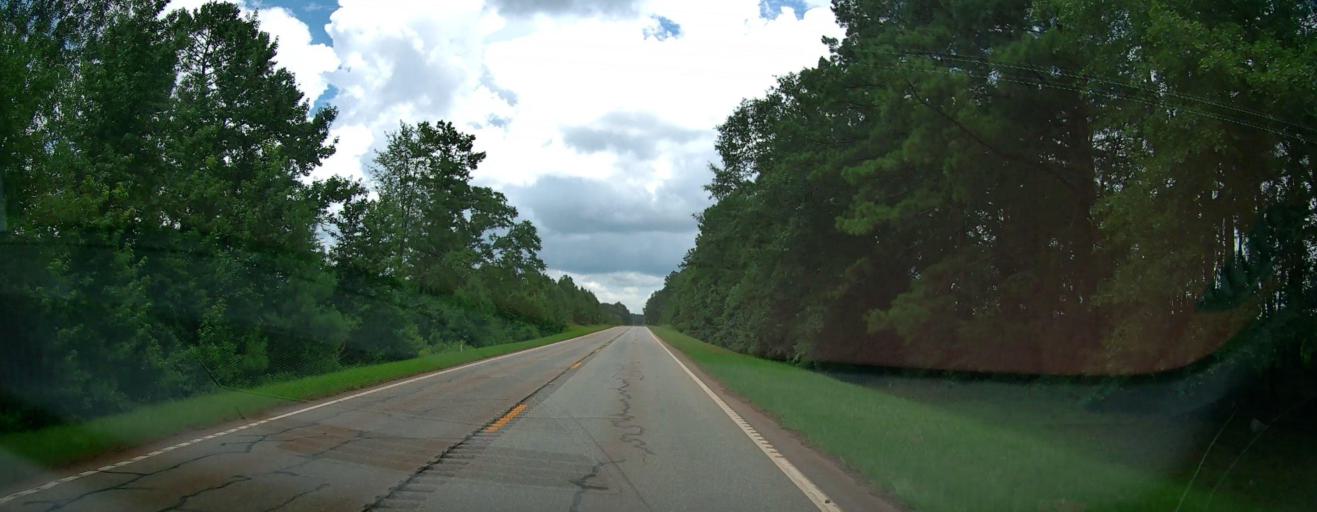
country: US
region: Georgia
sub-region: Pulaski County
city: Hawkinsville
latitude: 32.3693
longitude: -83.5424
